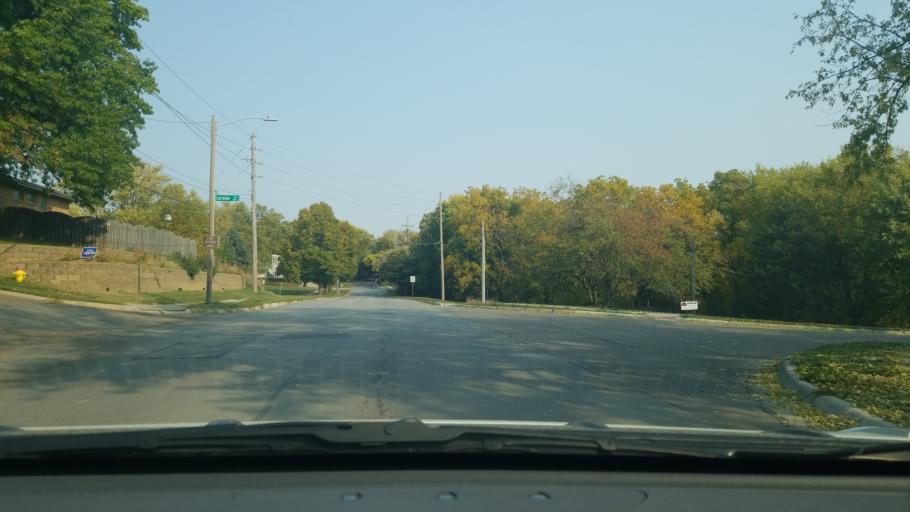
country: US
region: Nebraska
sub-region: Sarpy County
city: Bellevue
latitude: 41.1582
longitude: -95.9091
